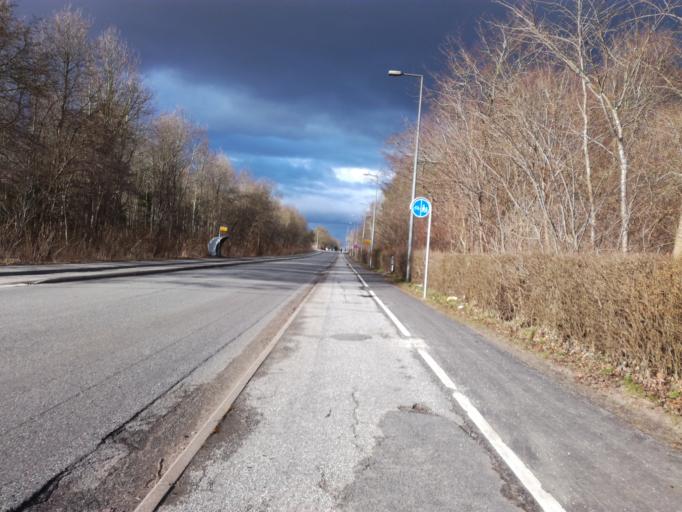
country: DK
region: South Denmark
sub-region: Fredericia Kommune
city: Fredericia
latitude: 55.5849
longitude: 9.7673
